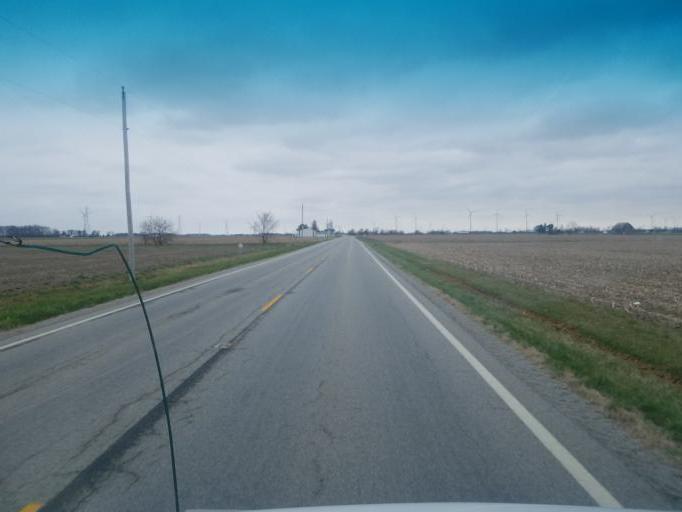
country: US
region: Ohio
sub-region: Van Wert County
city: Van Wert
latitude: 40.9320
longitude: -84.4888
